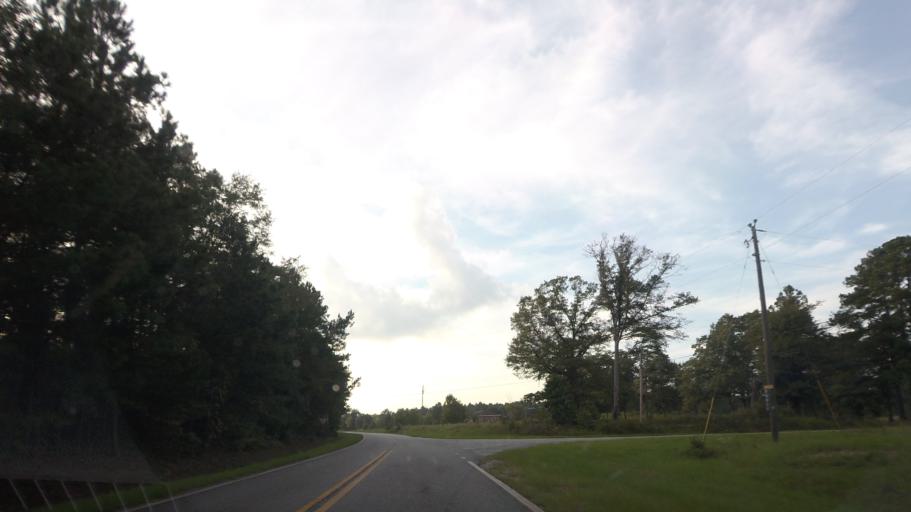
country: US
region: Georgia
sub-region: Wilkinson County
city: Gordon
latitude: 32.8651
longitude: -83.4648
